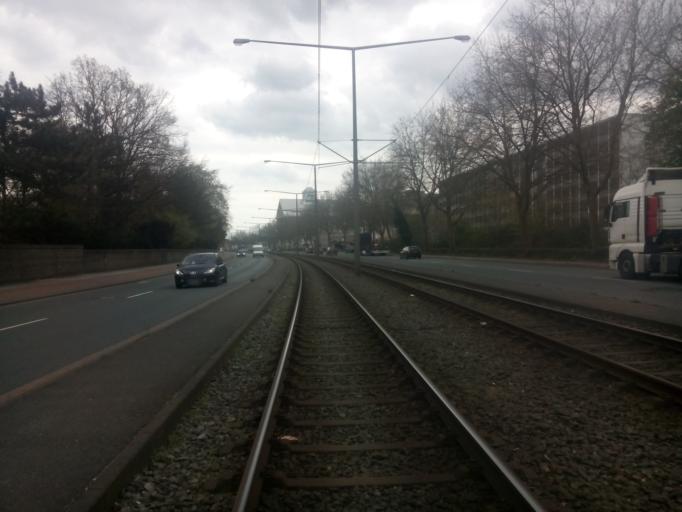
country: DE
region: Bremen
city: Bremen
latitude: 53.1051
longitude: 8.7679
